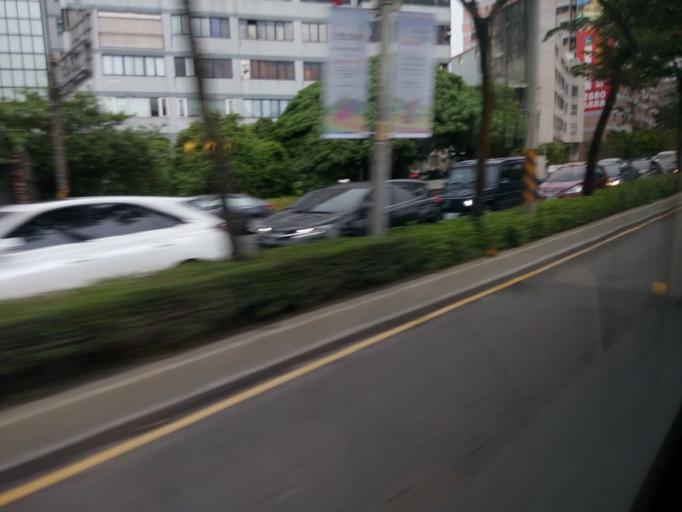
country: TW
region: Taipei
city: Taipei
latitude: 25.0566
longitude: 121.6342
